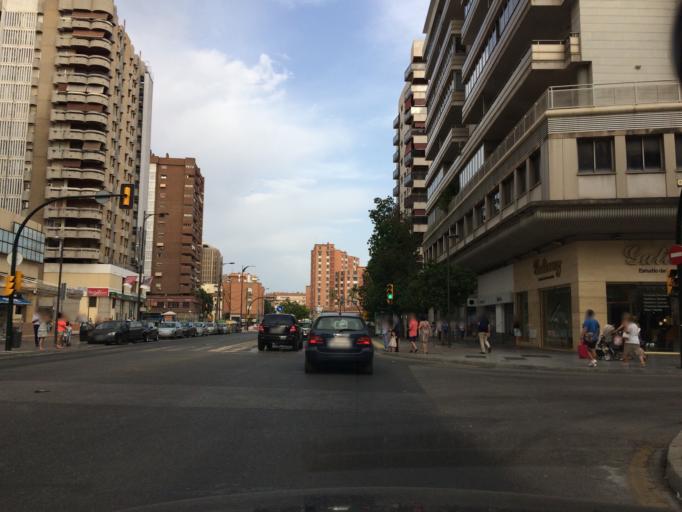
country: ES
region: Andalusia
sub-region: Provincia de Malaga
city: Malaga
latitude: 36.7162
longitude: -4.4313
